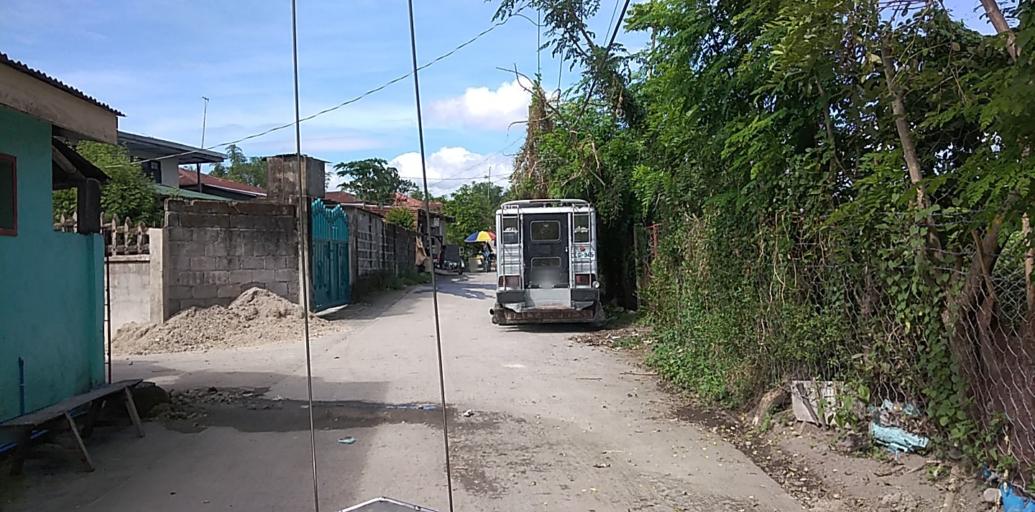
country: PH
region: Central Luzon
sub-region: Province of Pampanga
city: Porac
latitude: 15.0776
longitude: 120.5345
